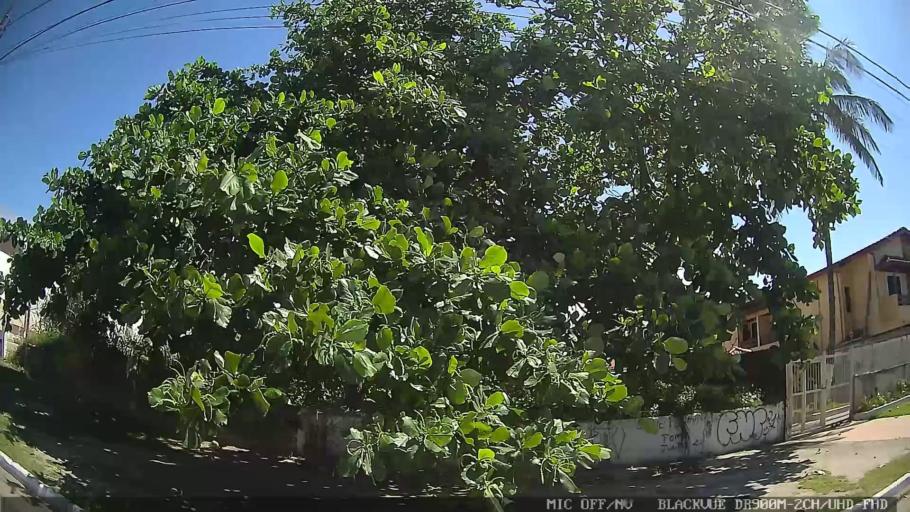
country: BR
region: Sao Paulo
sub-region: Peruibe
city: Peruibe
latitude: -24.3231
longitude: -46.9940
